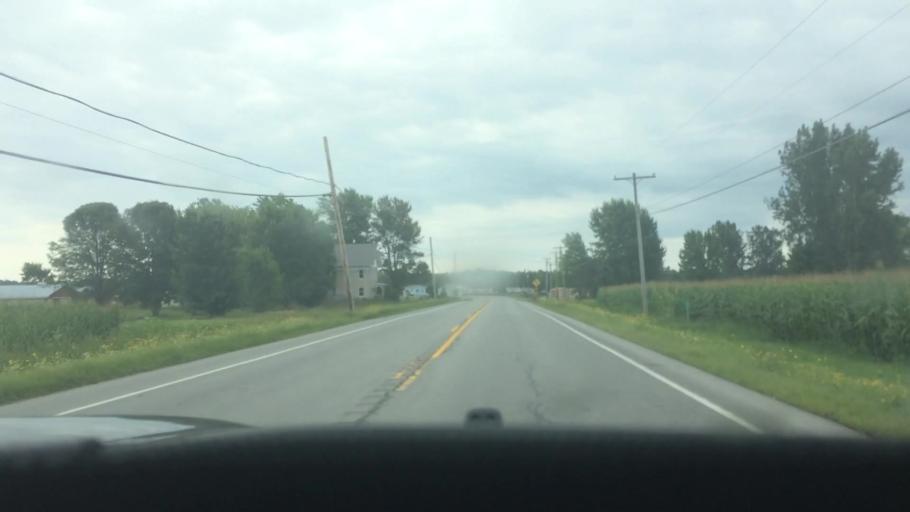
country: US
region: New York
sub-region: St. Lawrence County
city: Ogdensburg
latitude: 44.6661
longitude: -75.4680
